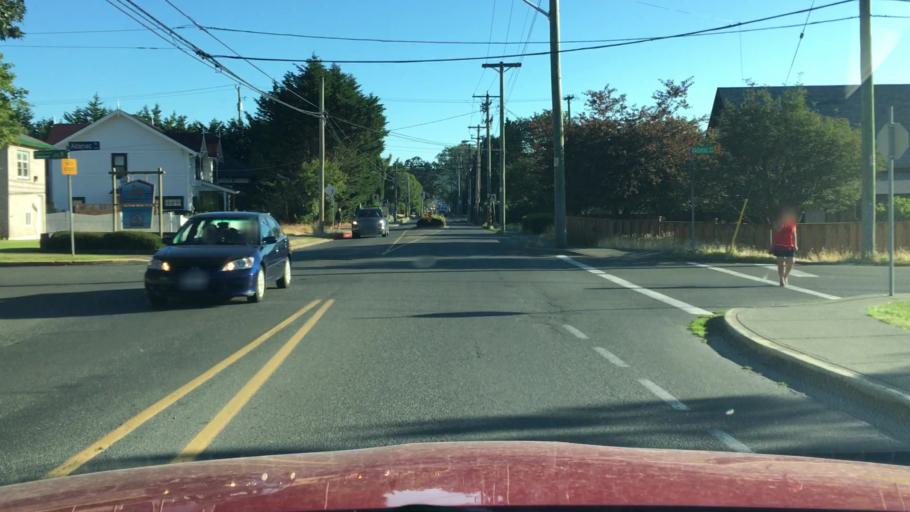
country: CA
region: British Columbia
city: Oak Bay
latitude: 48.4351
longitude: -123.3289
